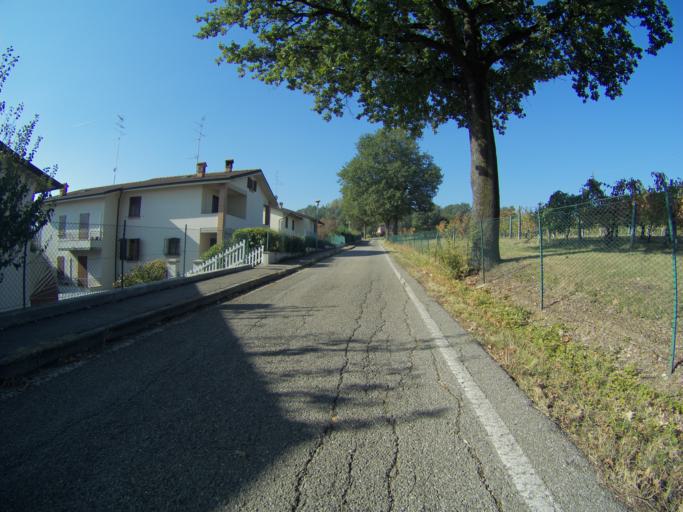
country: IT
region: Emilia-Romagna
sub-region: Provincia di Reggio Emilia
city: Puianello
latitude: 44.6248
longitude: 10.5595
